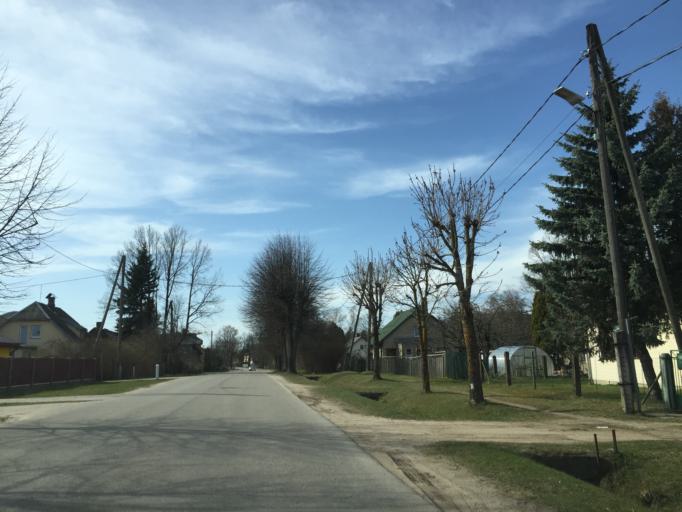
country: LV
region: Ogre
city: Ogre
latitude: 56.8191
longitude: 24.5839
